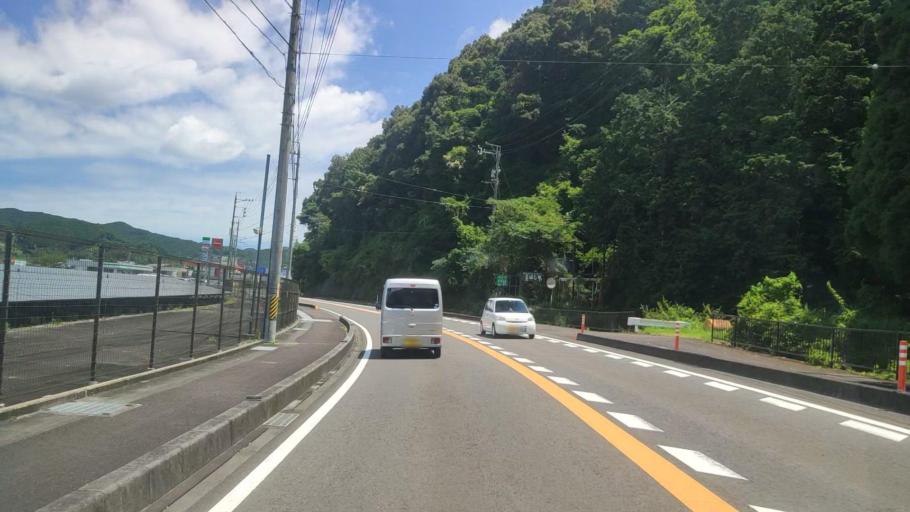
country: JP
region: Mie
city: Owase
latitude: 34.1151
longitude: 136.2207
